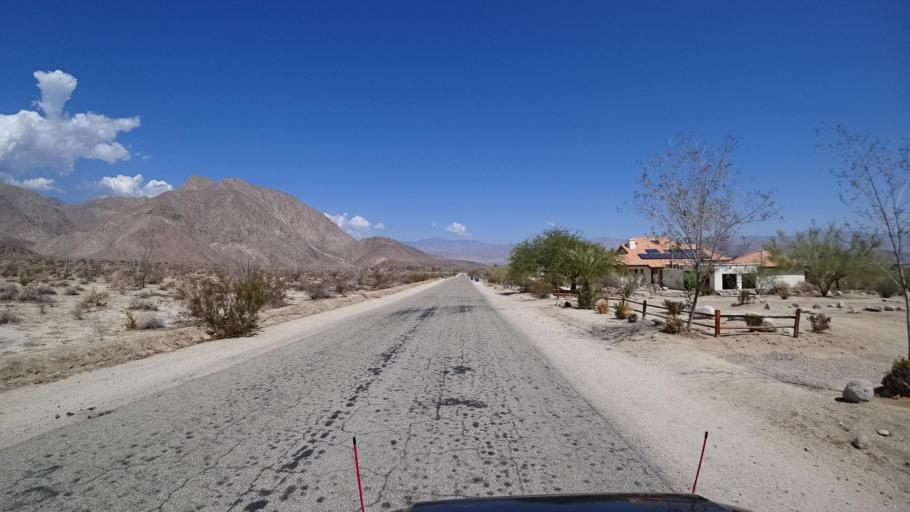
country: US
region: California
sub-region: San Diego County
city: Borrego Springs
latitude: 33.2612
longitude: -116.3995
